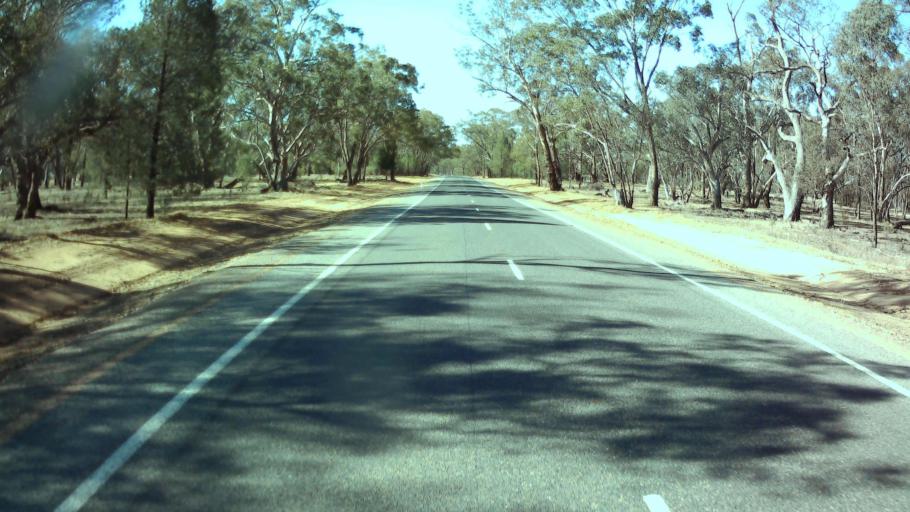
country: AU
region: New South Wales
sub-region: Weddin
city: Grenfell
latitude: -33.7619
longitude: 148.0820
